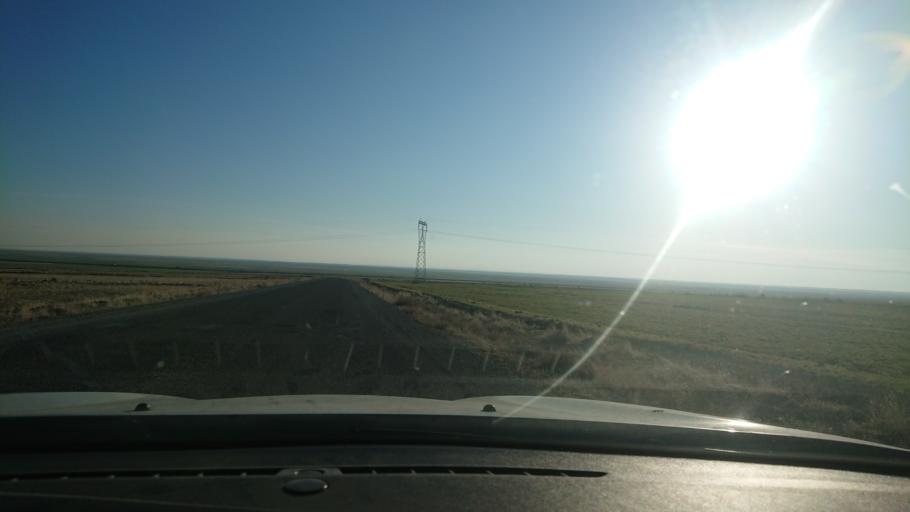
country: TR
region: Aksaray
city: Acipinar
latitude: 38.6740
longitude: 33.7291
